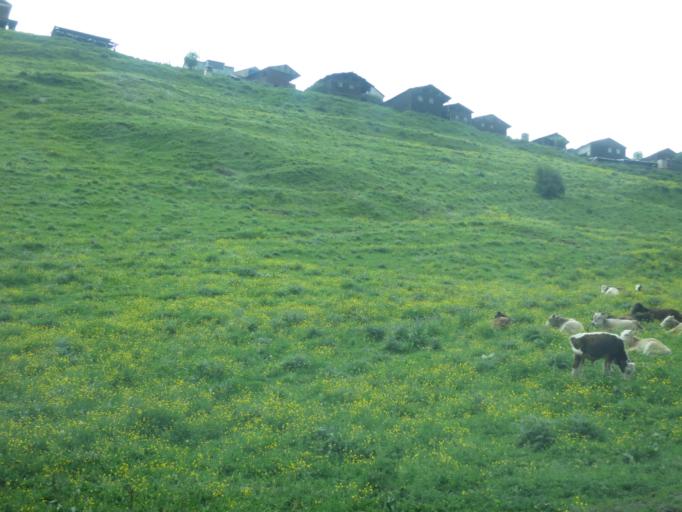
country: RU
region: Chechnya
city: Itum-Kali
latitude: 42.3742
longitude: 45.6631
